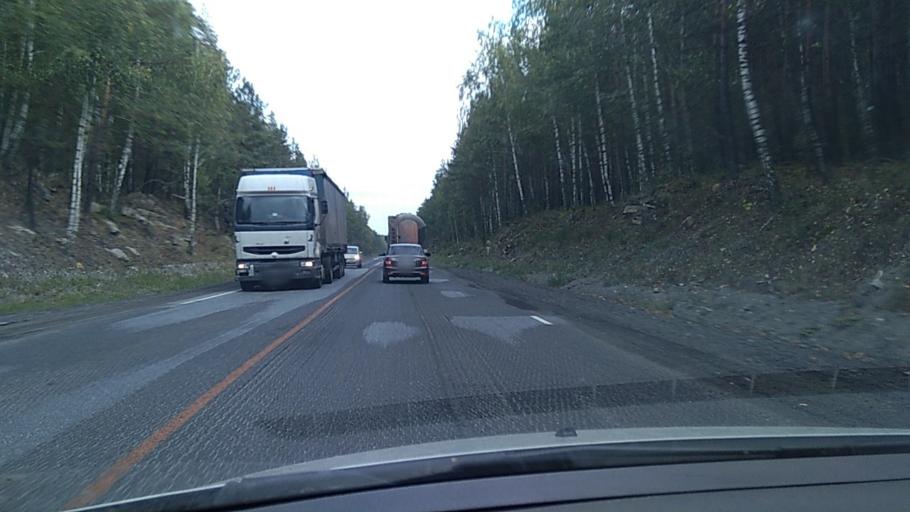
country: RU
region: Chelyabinsk
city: Miass
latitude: 54.9302
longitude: 60.1795
